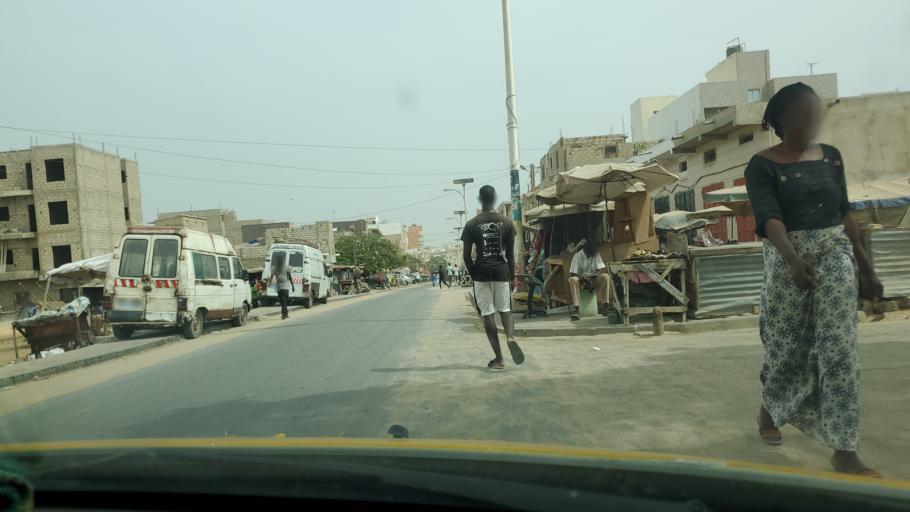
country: SN
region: Dakar
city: Pikine
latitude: 14.7730
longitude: -17.3944
